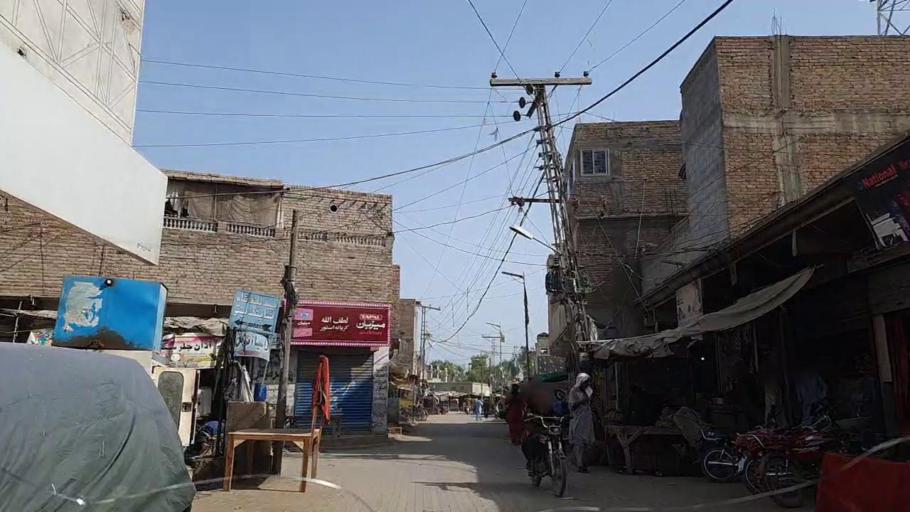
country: PK
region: Sindh
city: Kandiaro
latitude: 27.0593
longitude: 68.2077
